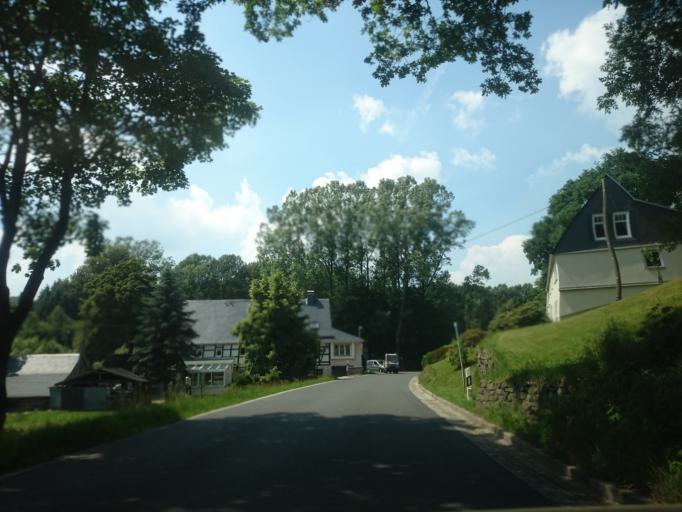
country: DE
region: Saxony
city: Oberschona
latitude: 50.8753
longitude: 13.2832
